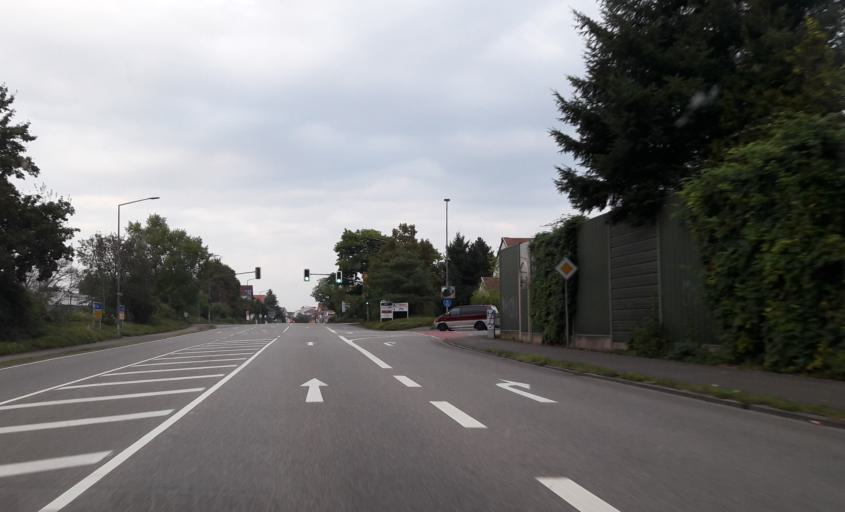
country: DE
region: Saarland
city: Homburg
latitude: 49.3099
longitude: 7.3335
